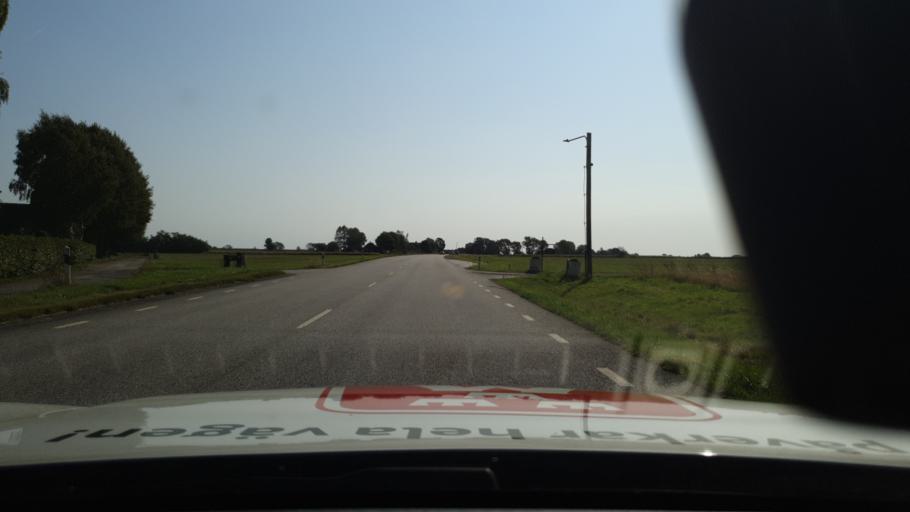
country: SE
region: Skane
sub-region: Kristianstads Kommun
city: Norra Asum
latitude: 55.9780
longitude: 14.1725
